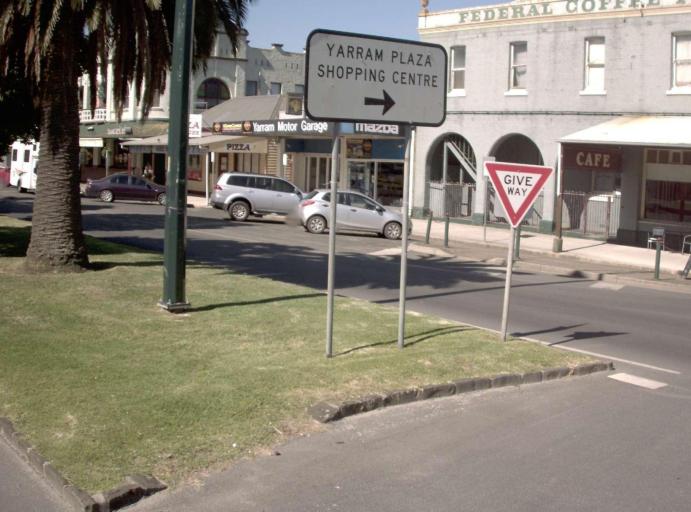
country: AU
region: Victoria
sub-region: Latrobe
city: Traralgon
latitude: -38.5651
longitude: 146.6755
